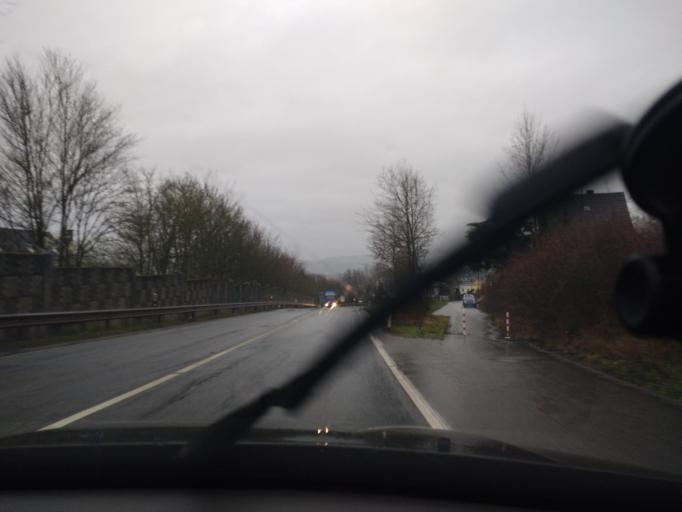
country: DE
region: Rheinland-Pfalz
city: Trier
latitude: 49.7214
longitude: 6.6295
